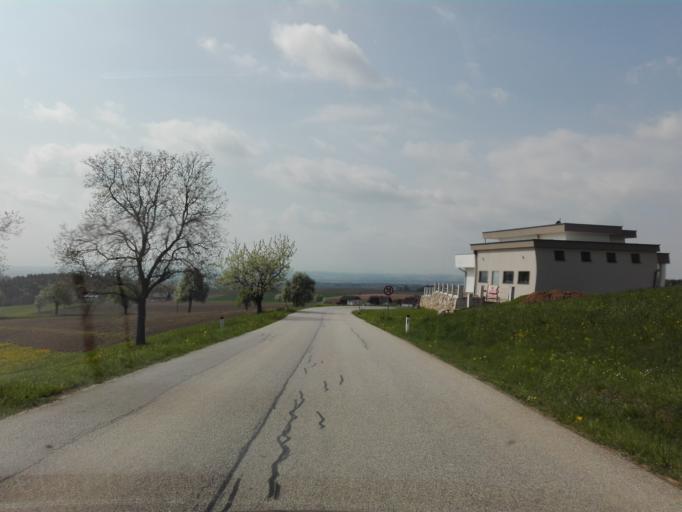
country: AT
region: Upper Austria
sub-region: Politischer Bezirk Perg
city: Perg
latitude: 48.2439
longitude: 14.7008
